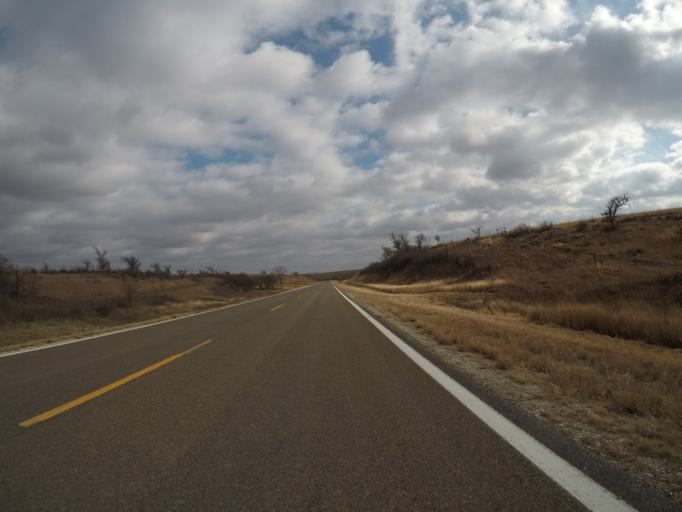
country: US
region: Kansas
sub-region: Wabaunsee County
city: Alma
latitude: 38.8684
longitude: -96.3121
